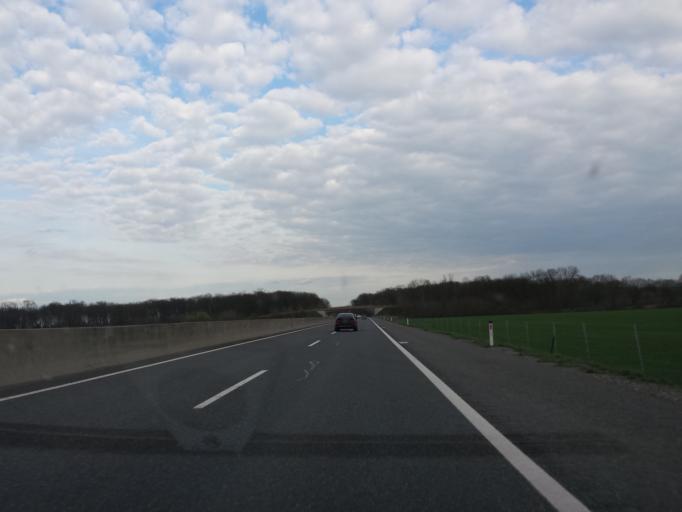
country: AT
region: Lower Austria
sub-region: Politischer Bezirk Korneuburg
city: Stetteldorf am Wagram
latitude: 48.3596
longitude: 15.9899
